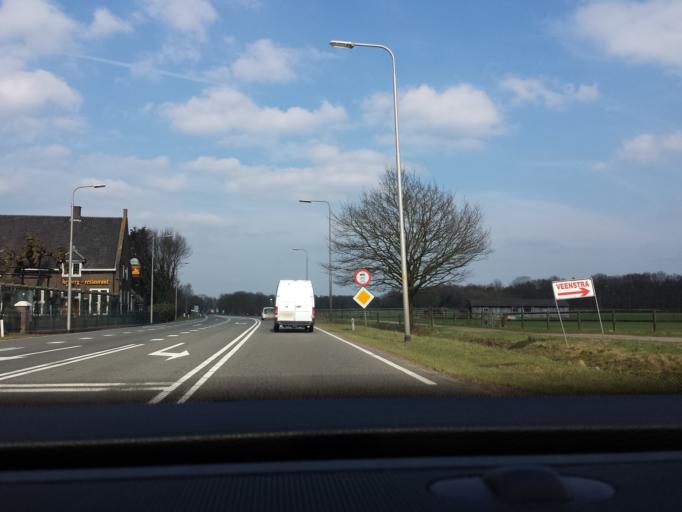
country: NL
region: Gelderland
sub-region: Oude IJsselstreek
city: Varsseveld
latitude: 51.9654
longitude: 6.5012
